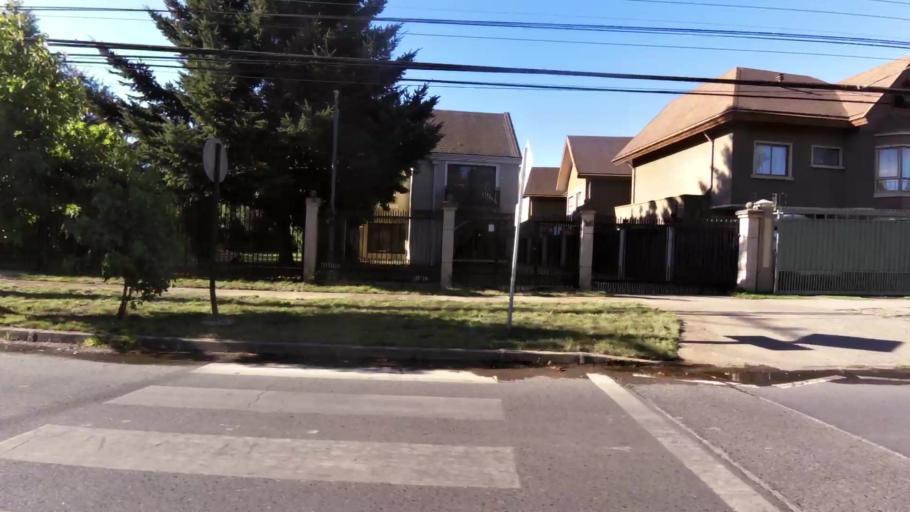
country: CL
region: Biobio
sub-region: Provincia de Concepcion
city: Concepcion
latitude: -36.8368
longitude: -73.1072
